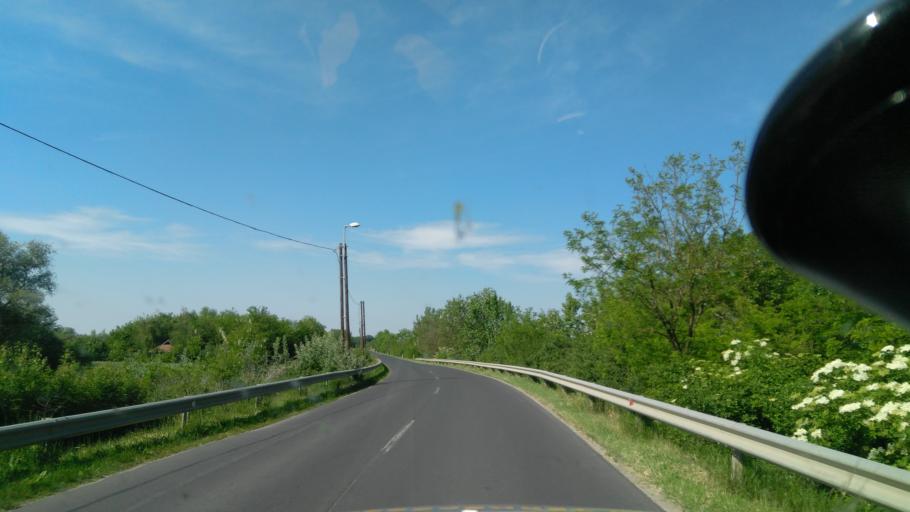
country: HU
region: Bekes
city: Gyula
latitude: 46.6673
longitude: 21.2990
